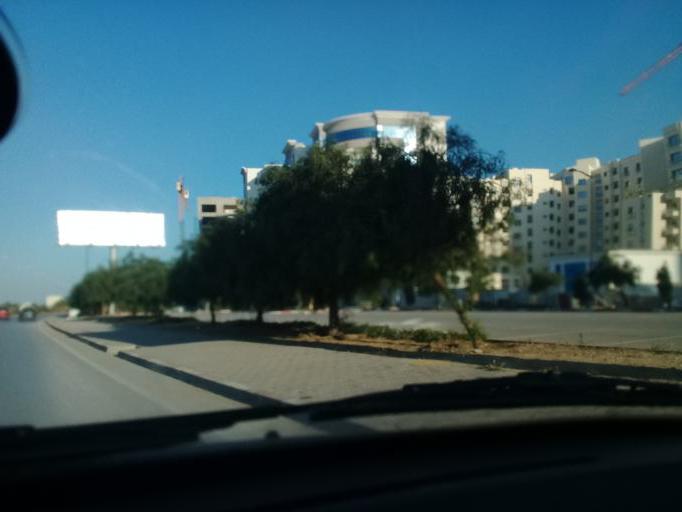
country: TN
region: Tunis
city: La Goulette
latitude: 36.8497
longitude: 10.2762
